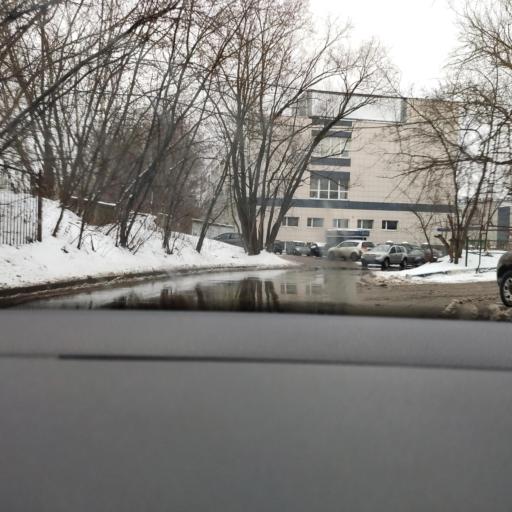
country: RU
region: Moscow
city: Metrogorodok
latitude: 55.8248
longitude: 37.7789
